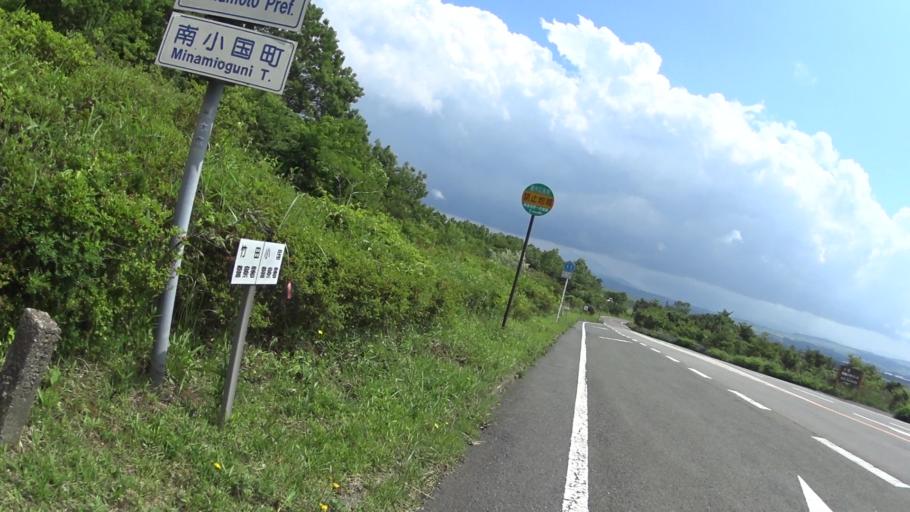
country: JP
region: Kumamoto
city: Aso
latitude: 33.0760
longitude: 131.1955
